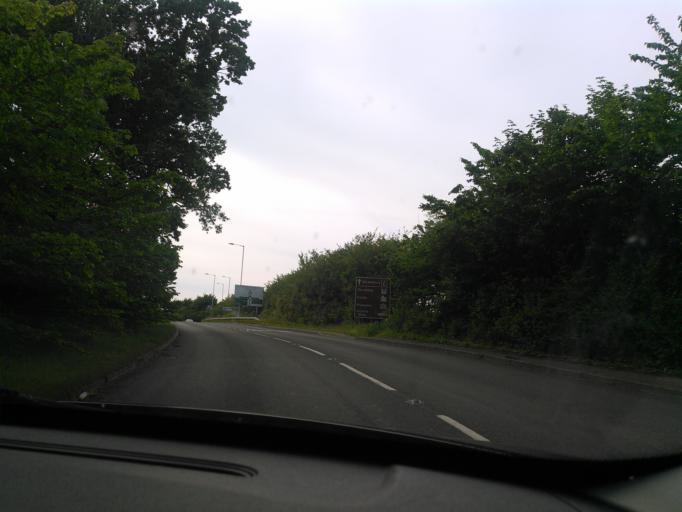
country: GB
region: England
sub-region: Shropshire
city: Astley
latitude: 52.7279
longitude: -2.7064
